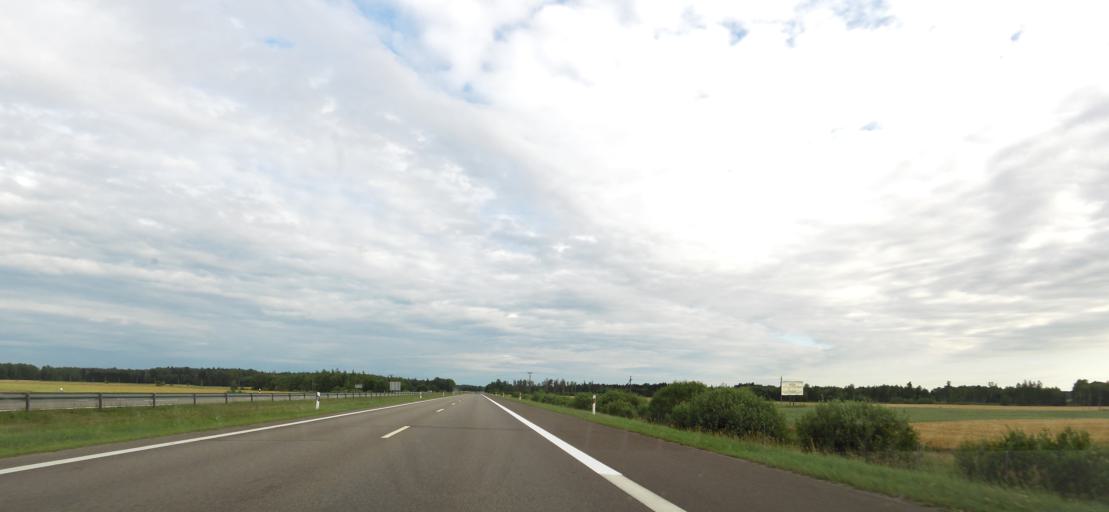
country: LT
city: Sirvintos
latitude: 55.0638
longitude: 24.8864
